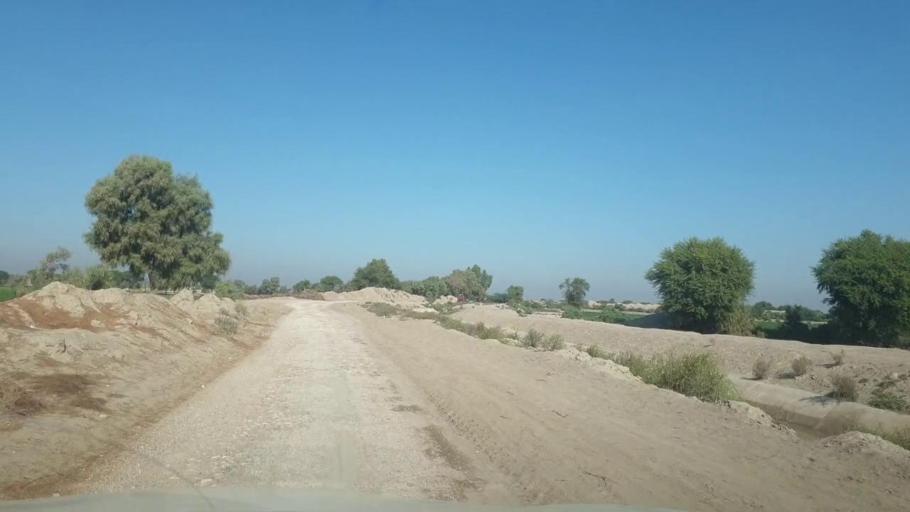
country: PK
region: Sindh
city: Bhan
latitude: 26.5589
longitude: 67.6300
